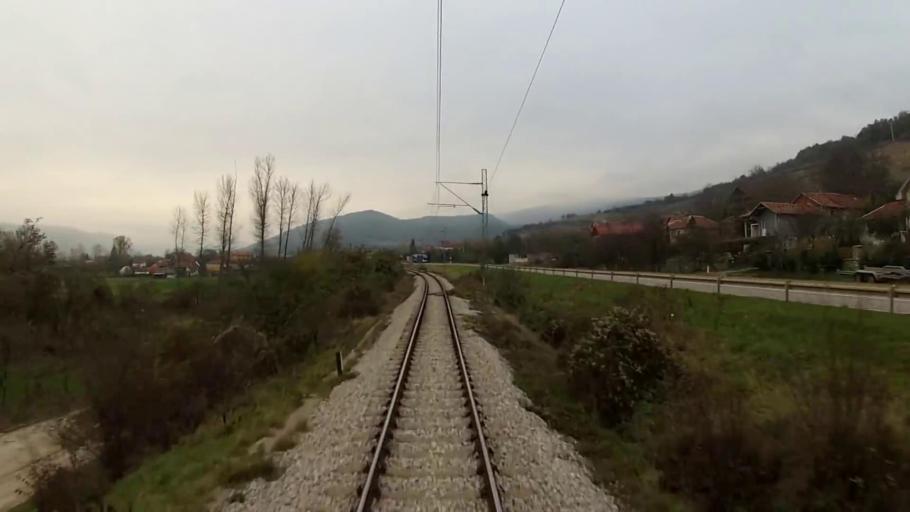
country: RS
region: Central Serbia
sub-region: Pirotski Okrug
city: Dimitrovgrad
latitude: 43.0054
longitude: 22.8074
